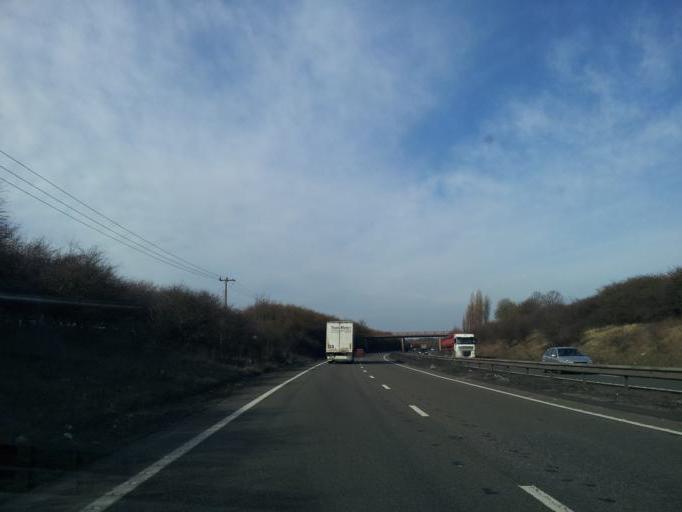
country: GB
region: England
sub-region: Nottinghamshire
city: Newark on Trent
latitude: 53.0407
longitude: -0.7777
